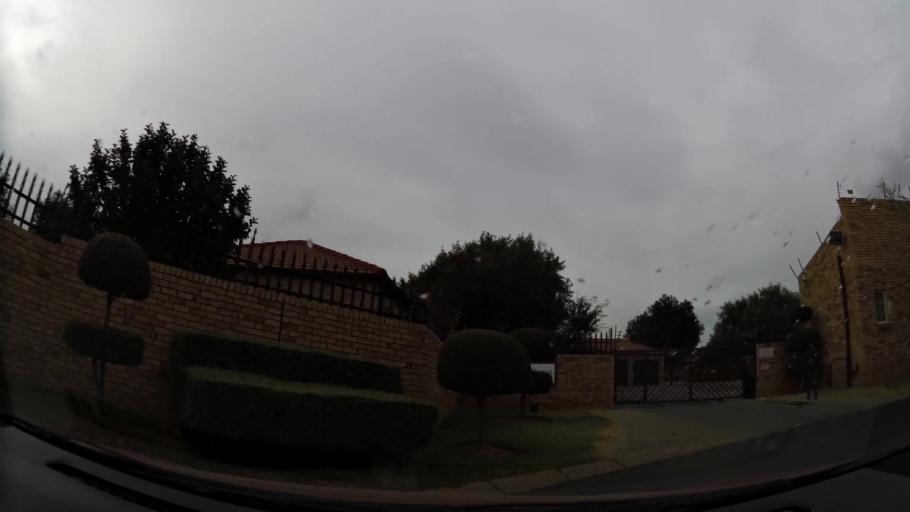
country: ZA
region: Gauteng
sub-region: City of Johannesburg Metropolitan Municipality
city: Roodepoort
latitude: -26.1028
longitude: 27.9020
